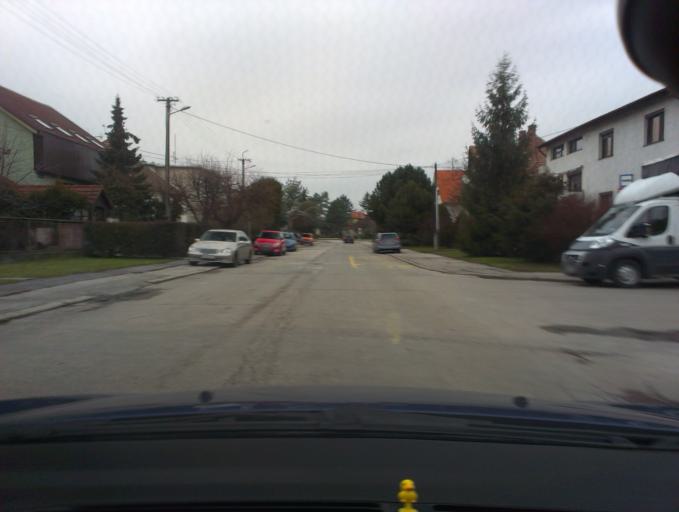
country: SK
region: Trnavsky
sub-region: Okres Trnava
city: Piestany
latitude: 48.5832
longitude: 17.8316
